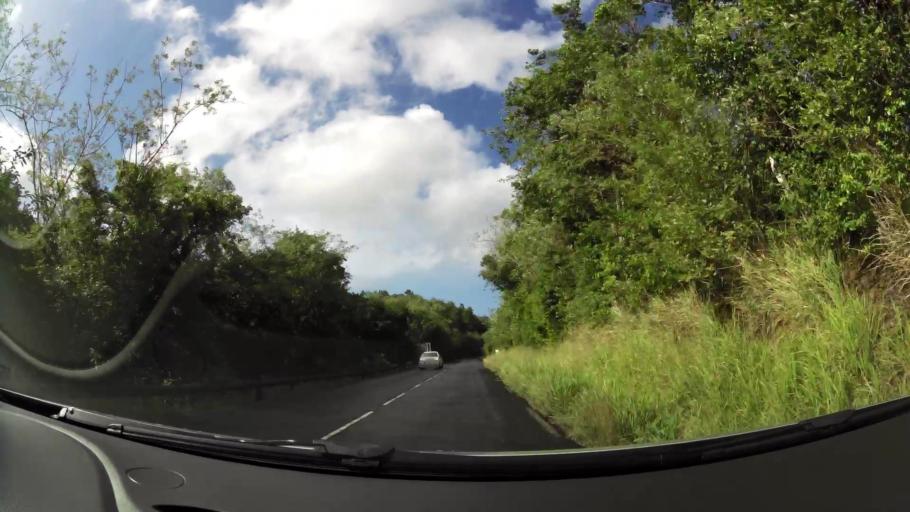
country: MQ
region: Martinique
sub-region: Martinique
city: Les Trois-Ilets
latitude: 14.5356
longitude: -61.0493
